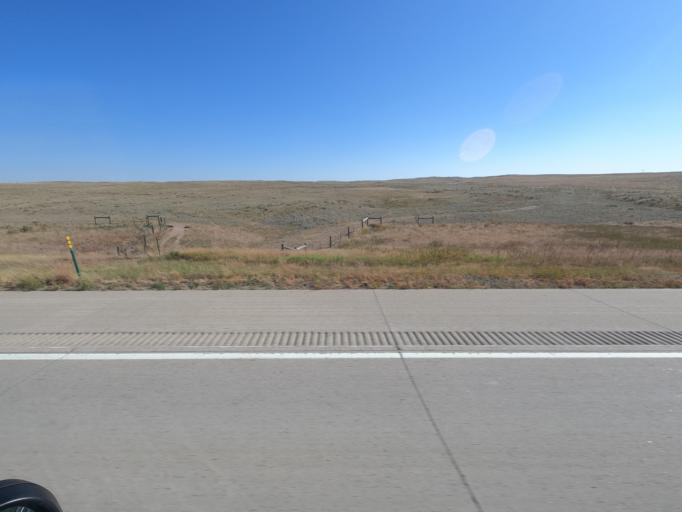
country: US
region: Nebraska
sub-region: Deuel County
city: Chappell
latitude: 40.9239
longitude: -102.4495
